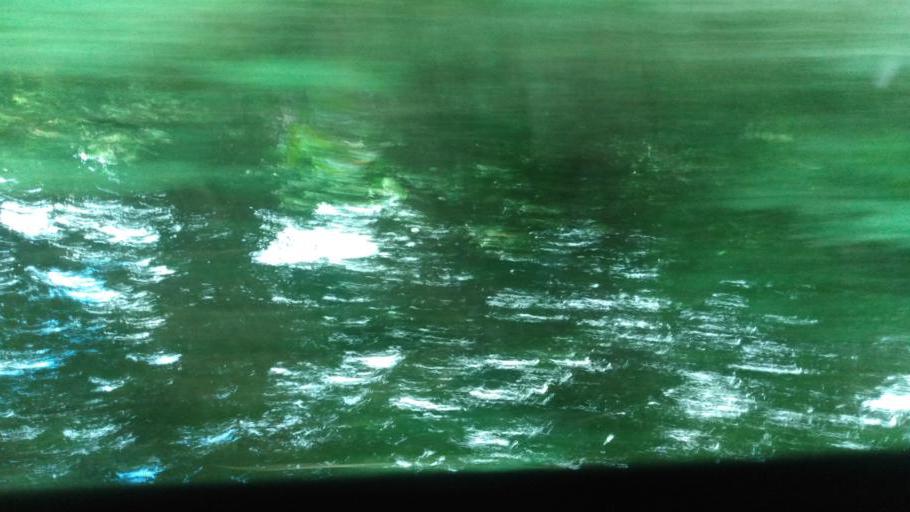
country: BR
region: Pernambuco
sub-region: Quipapa
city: Quipapa
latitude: -8.7794
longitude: -35.9478
